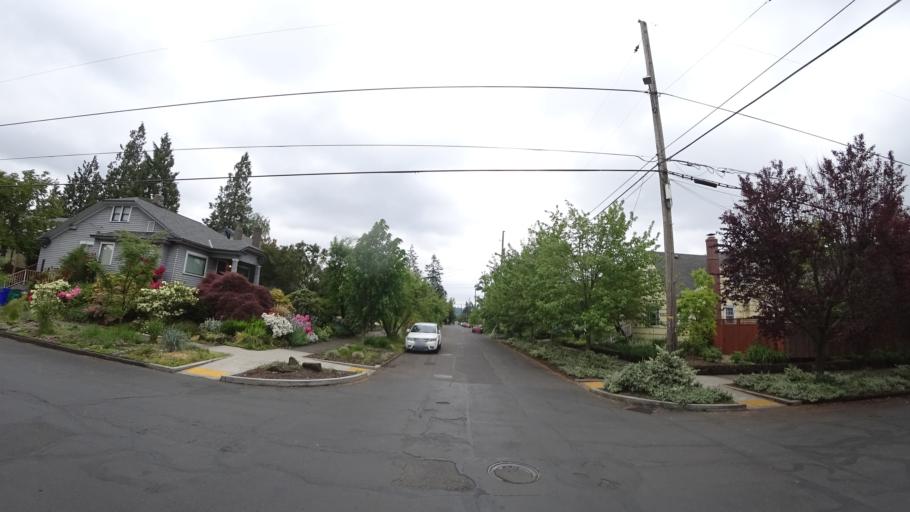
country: US
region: Oregon
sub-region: Multnomah County
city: Portland
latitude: 45.5454
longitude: -122.6067
